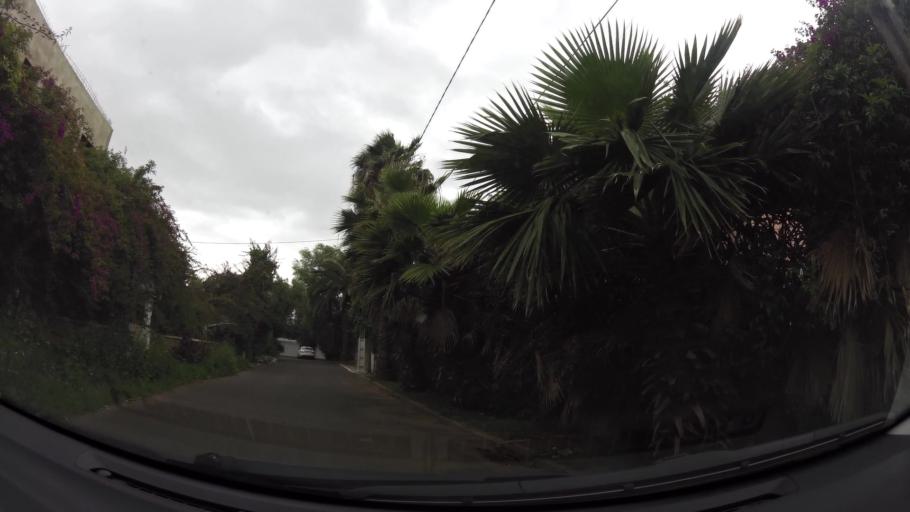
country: MA
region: Grand Casablanca
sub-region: Casablanca
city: Casablanca
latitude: 33.5792
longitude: -7.6568
